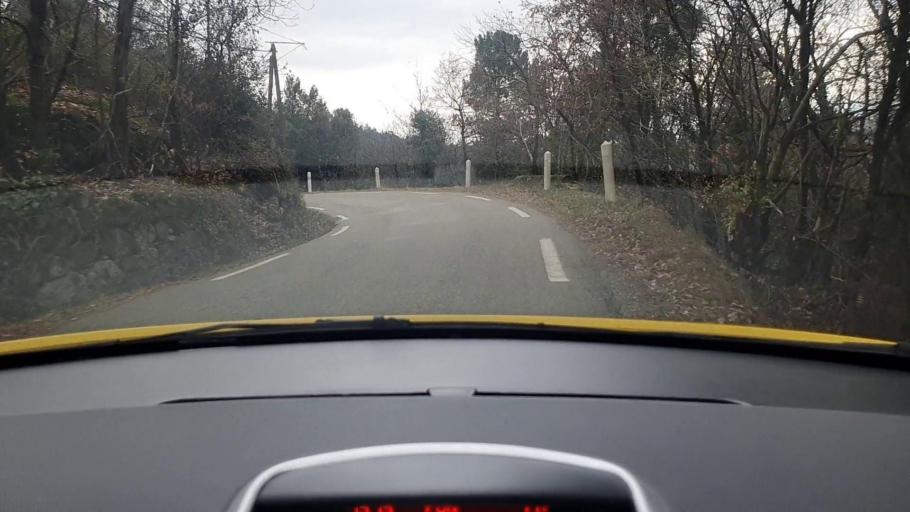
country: FR
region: Languedoc-Roussillon
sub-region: Departement du Gard
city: Besseges
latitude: 44.3493
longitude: 4.0199
